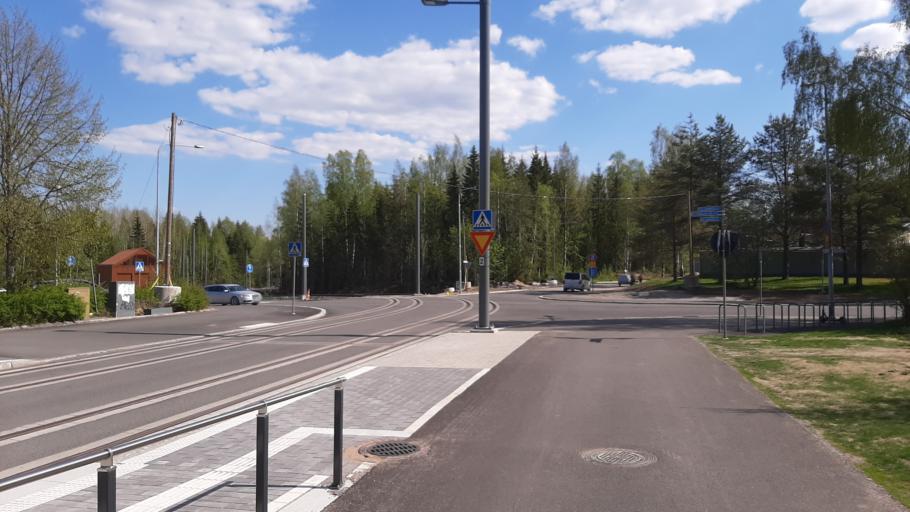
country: FI
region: Pirkanmaa
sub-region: Tampere
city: Tampere
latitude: 61.4426
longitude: 23.8585
